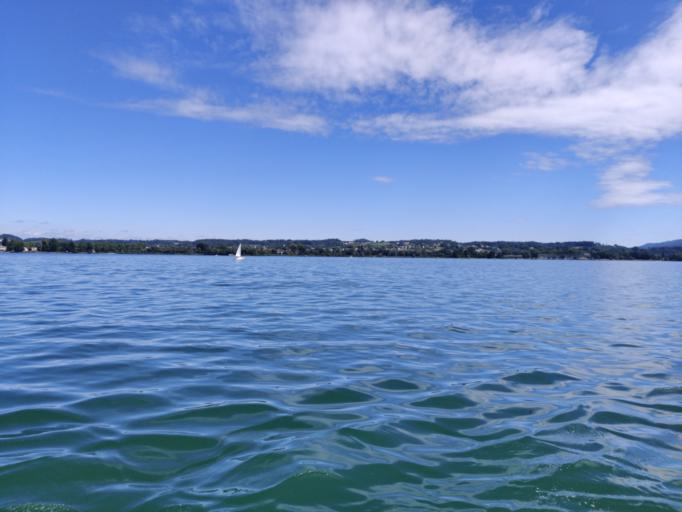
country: DE
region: Bavaria
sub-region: Swabia
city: Lindau
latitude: 47.5384
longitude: 9.7006
